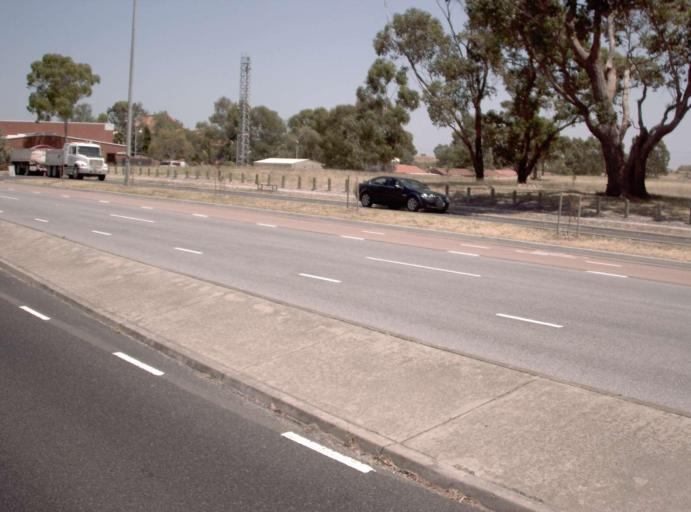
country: AU
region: Victoria
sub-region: Greater Dandenong
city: Springvale South
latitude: -37.9716
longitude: 145.1484
